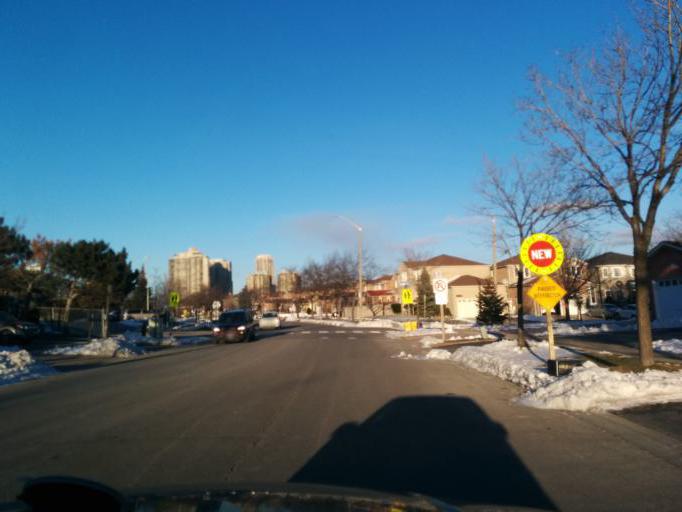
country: CA
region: Ontario
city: Mississauga
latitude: 43.5959
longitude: -79.6570
